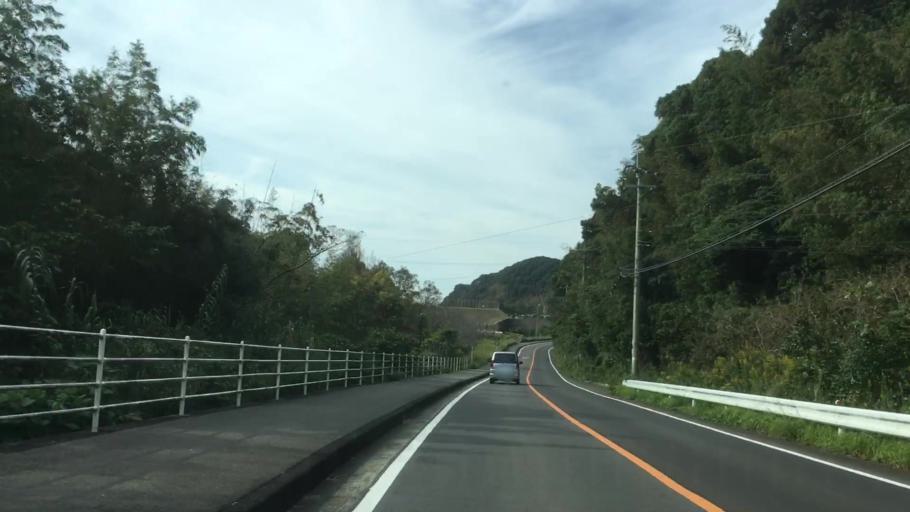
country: JP
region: Nagasaki
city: Sasebo
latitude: 33.0333
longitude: 129.6062
